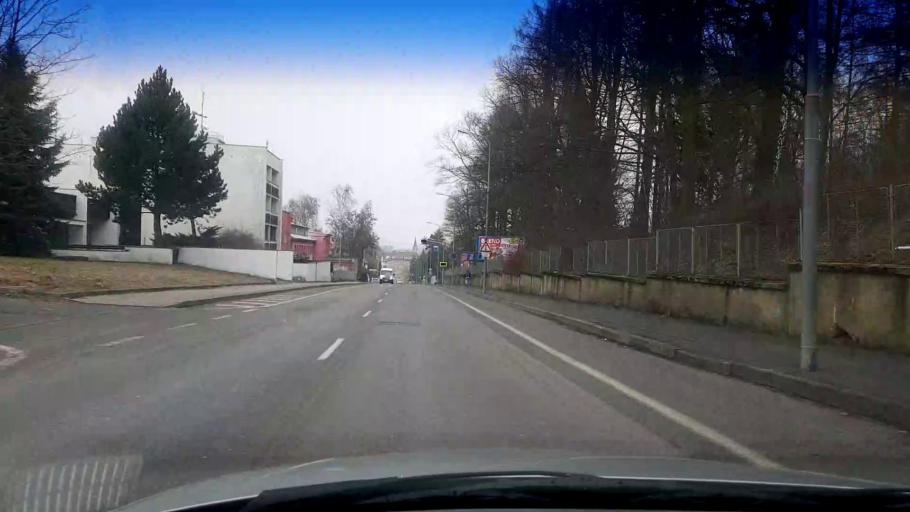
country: CZ
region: Karlovarsky
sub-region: Okres Cheb
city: Cheb
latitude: 50.0697
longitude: 12.3632
